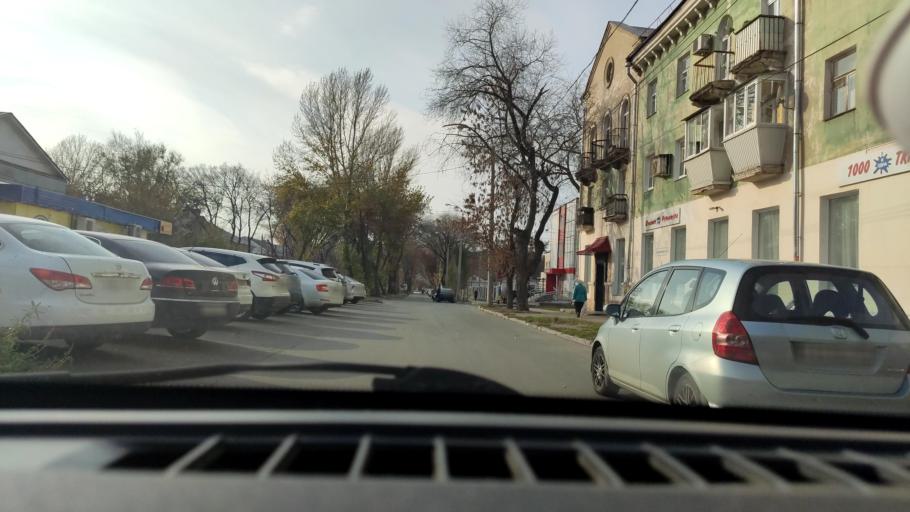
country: RU
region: Samara
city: Samara
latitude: 53.1940
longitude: 50.1307
